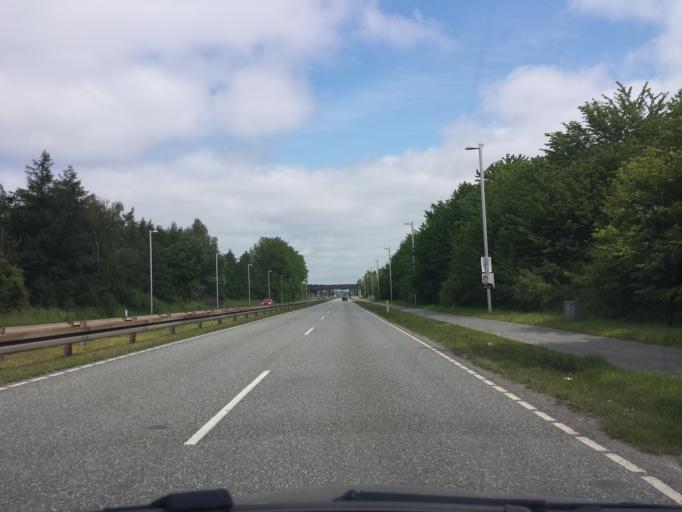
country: DK
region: Capital Region
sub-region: Glostrup Kommune
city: Glostrup
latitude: 55.6867
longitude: 12.4013
